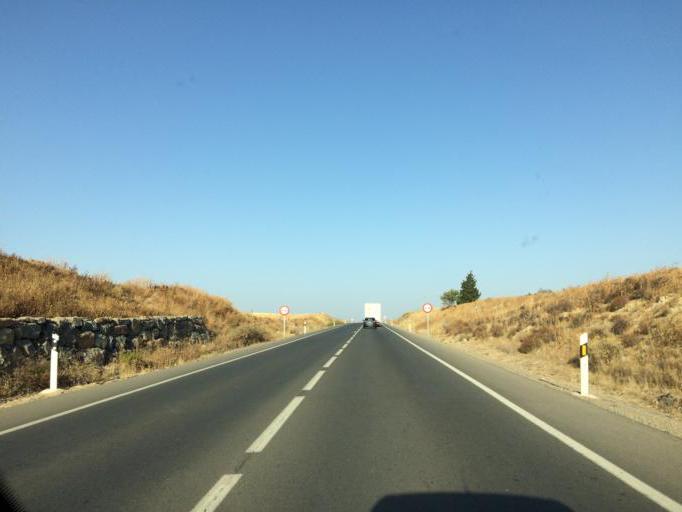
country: ES
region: Andalusia
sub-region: Provincia de Malaga
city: Campillos
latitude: 37.0511
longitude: -4.8129
